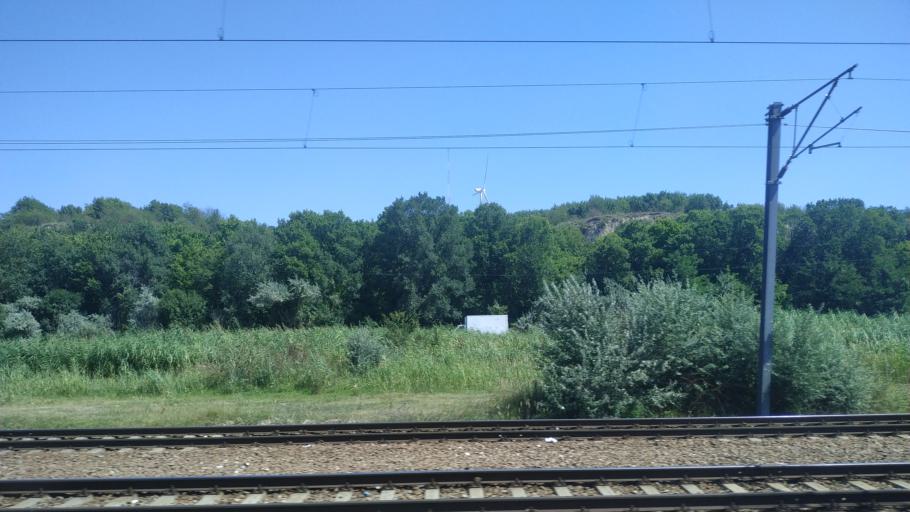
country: RO
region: Constanta
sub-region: Comuna Saligny
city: Saligny
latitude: 44.2919
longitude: 28.0748
